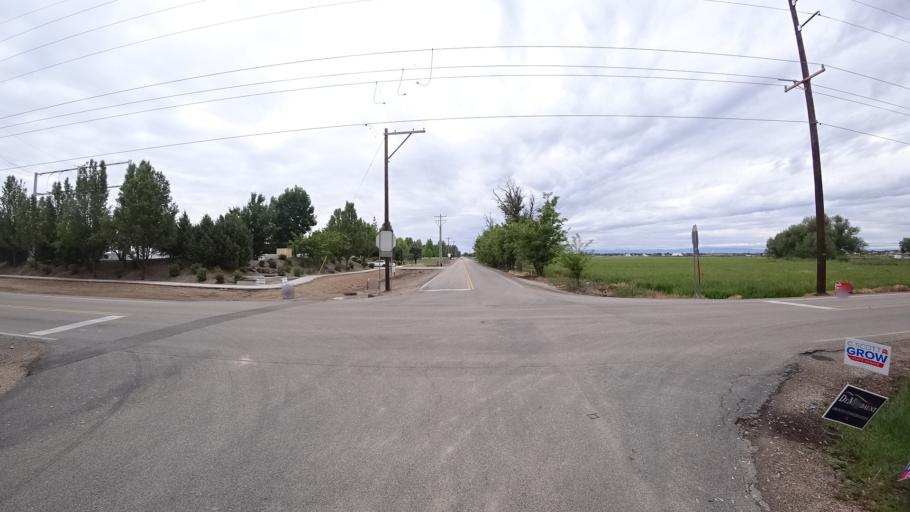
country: US
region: Idaho
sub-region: Ada County
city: Eagle
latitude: 43.7210
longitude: -116.4134
